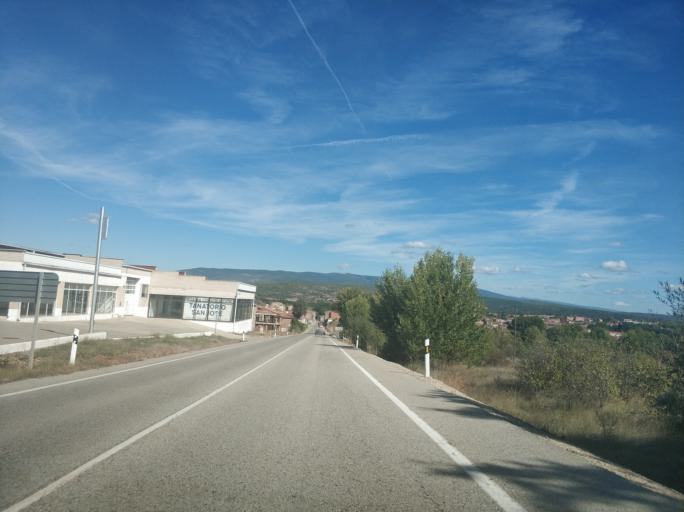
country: ES
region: Castille and Leon
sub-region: Provincia de Burgos
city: Salas de los Infantes
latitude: 42.0218
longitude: -3.2988
